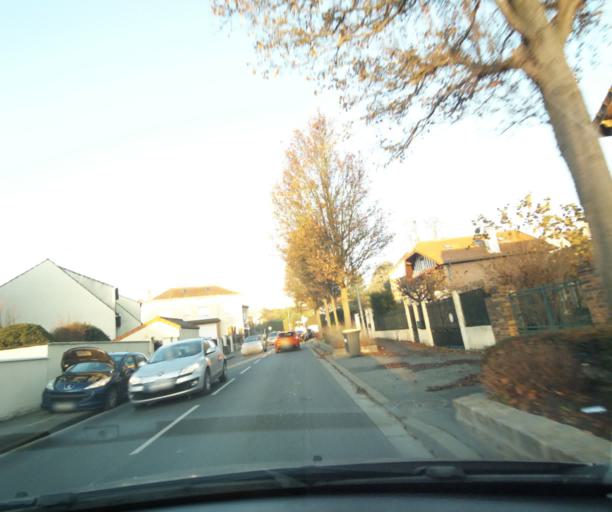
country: FR
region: Ile-de-France
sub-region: Departement de Seine-Saint-Denis
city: Gagny
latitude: 48.8751
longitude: 2.5267
